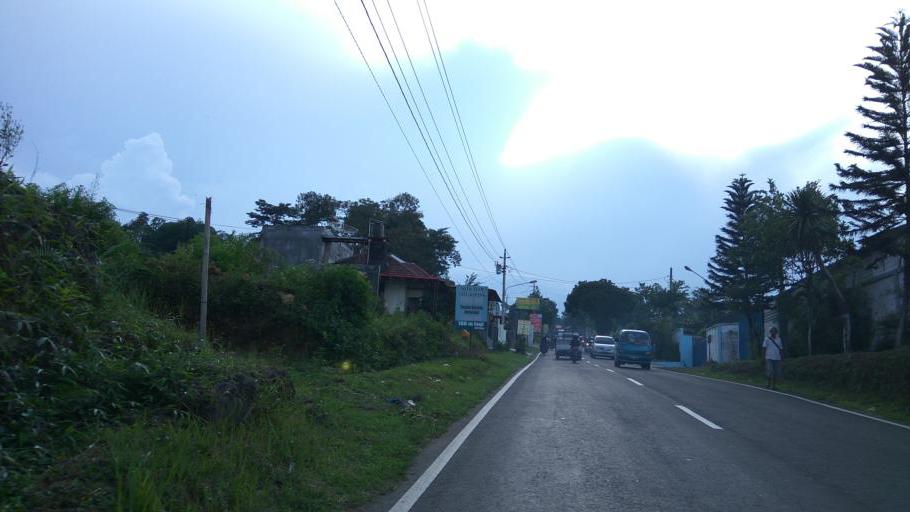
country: ID
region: Central Java
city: Salatiga
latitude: -7.3695
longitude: 110.4519
